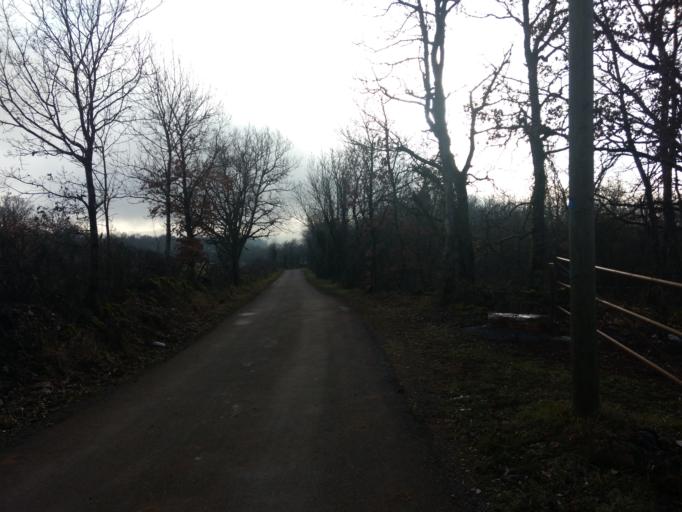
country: FR
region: Midi-Pyrenees
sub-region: Departement de l'Aveyron
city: Salles-la-Source
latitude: 44.4438
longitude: 2.5220
